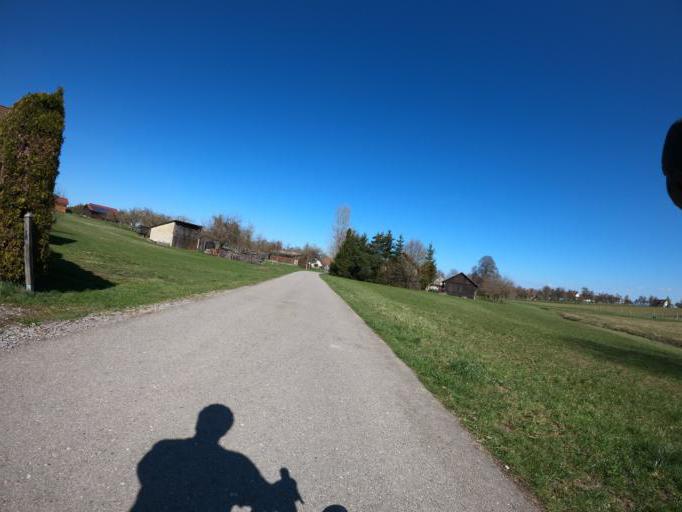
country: DE
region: Baden-Wuerttemberg
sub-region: Tuebingen Region
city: Haigerloch
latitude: 48.3867
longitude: 8.8371
